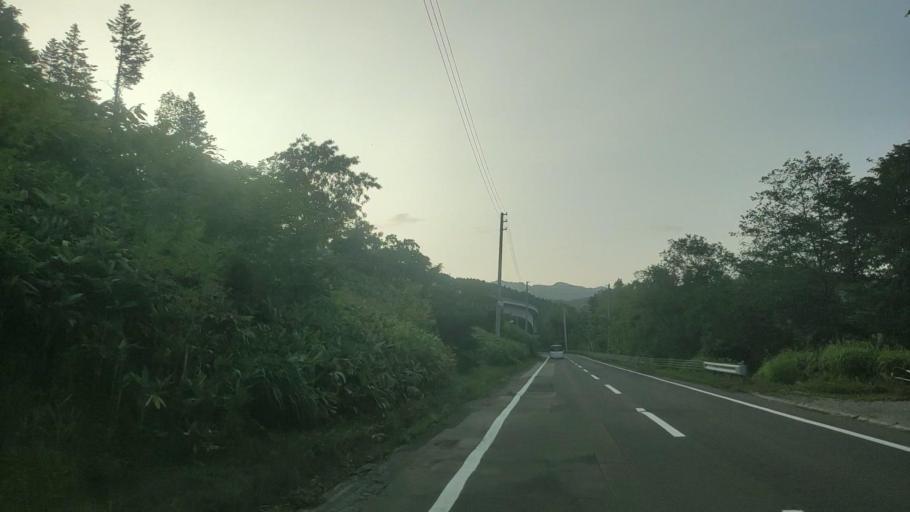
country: JP
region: Hokkaido
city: Bibai
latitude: 43.2260
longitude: 142.0450
